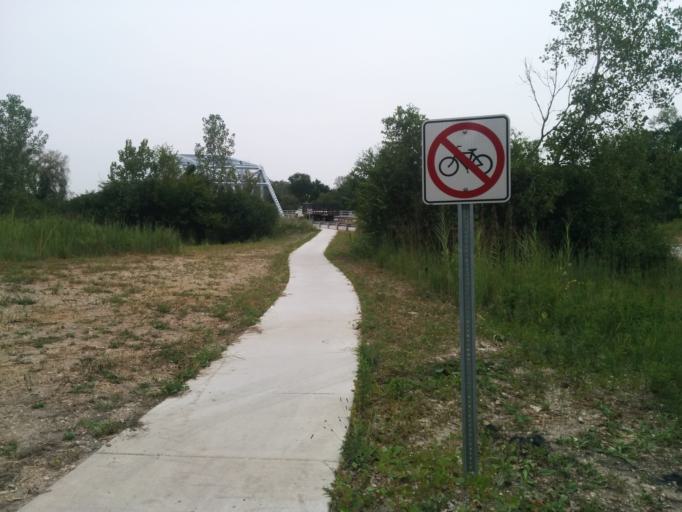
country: US
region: Illinois
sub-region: Cook County
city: Palos Park
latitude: 41.6865
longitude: -87.8752
